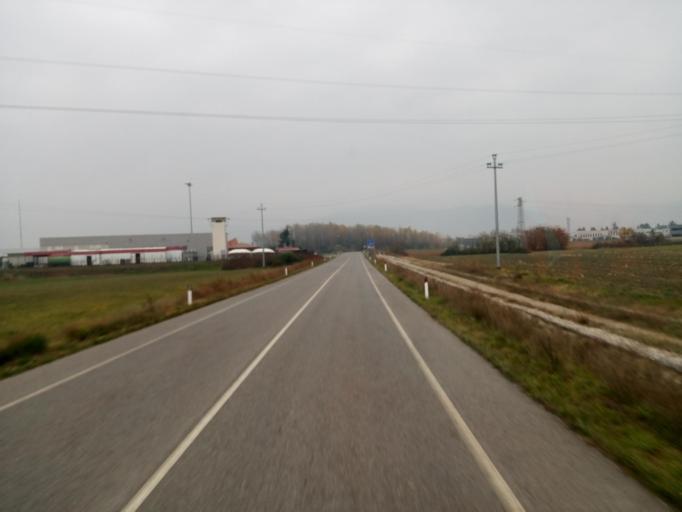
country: IT
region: Friuli Venezia Giulia
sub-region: Provincia di Udine
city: Moimacco
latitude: 46.0787
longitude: 13.3848
